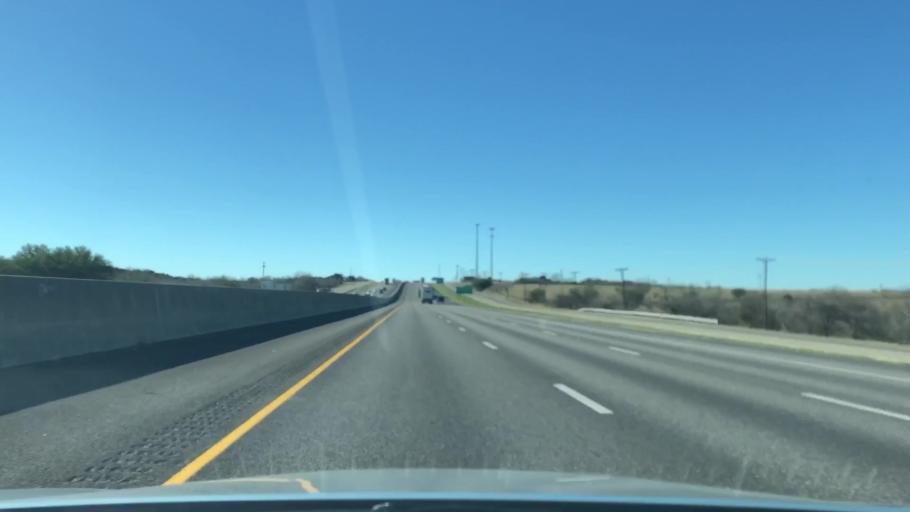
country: US
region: Texas
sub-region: Guadalupe County
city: Lake Dunlap
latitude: 29.7649
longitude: -98.0455
